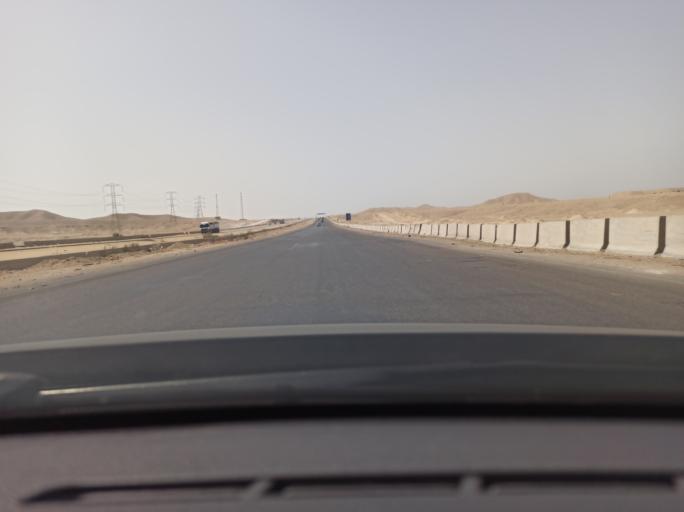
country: EG
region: Al Jizah
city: As Saff
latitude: 29.5476
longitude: 31.3944
